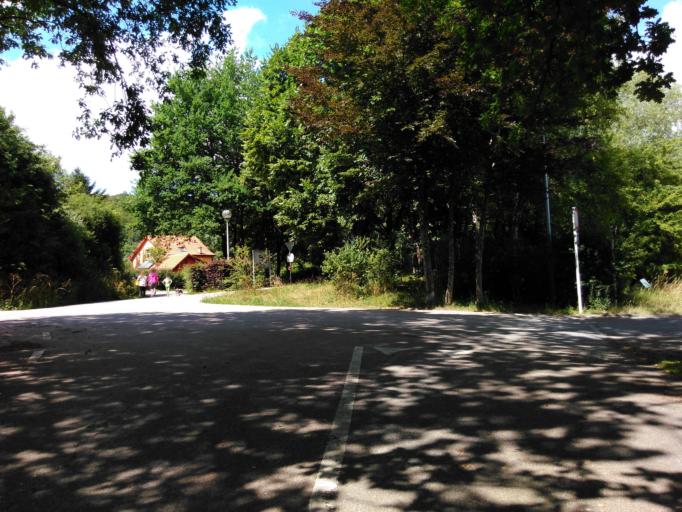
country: LU
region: Luxembourg
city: Hautcharage
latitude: 49.5808
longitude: 5.9061
